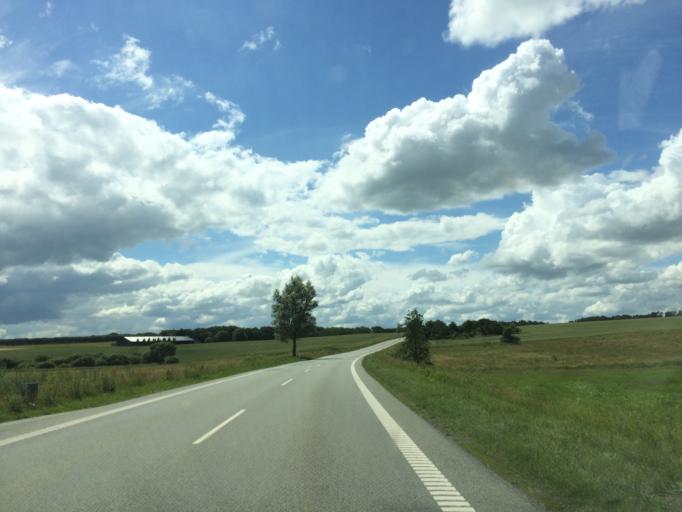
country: DK
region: North Denmark
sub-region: Mariagerfjord Kommune
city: Hobro
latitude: 56.6172
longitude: 9.7148
